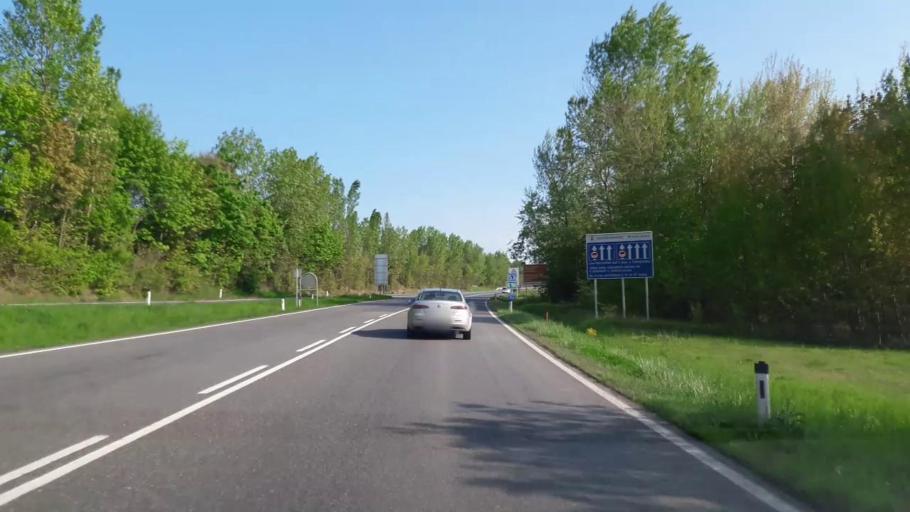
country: AT
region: Lower Austria
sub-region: Politischer Bezirk Hollabrunn
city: Hollabrunn
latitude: 48.5457
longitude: 16.0786
